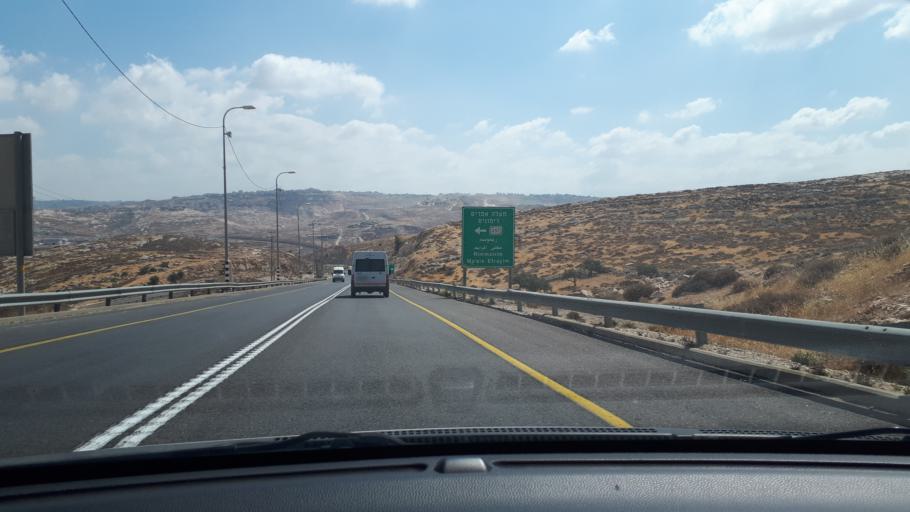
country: PS
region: West Bank
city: Mikhmas
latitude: 31.8817
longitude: 35.2709
